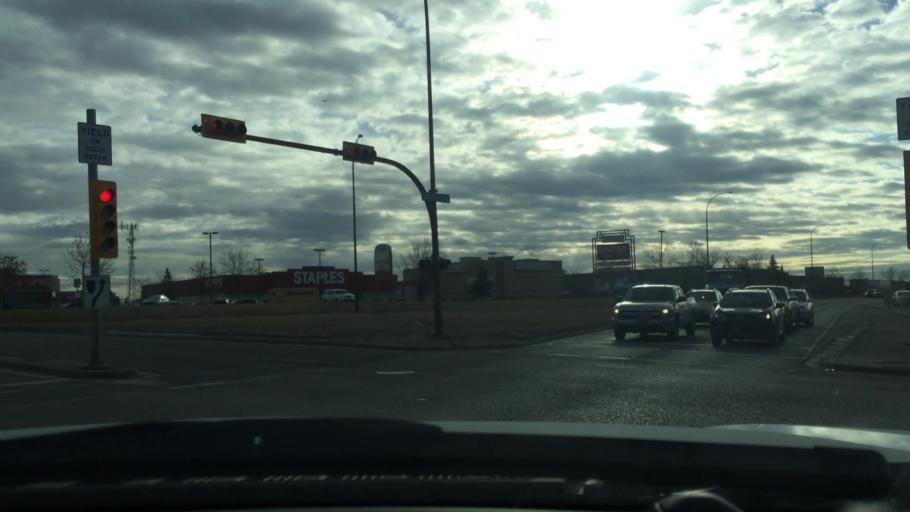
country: CA
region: Alberta
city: Calgary
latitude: 50.9988
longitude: -113.9843
